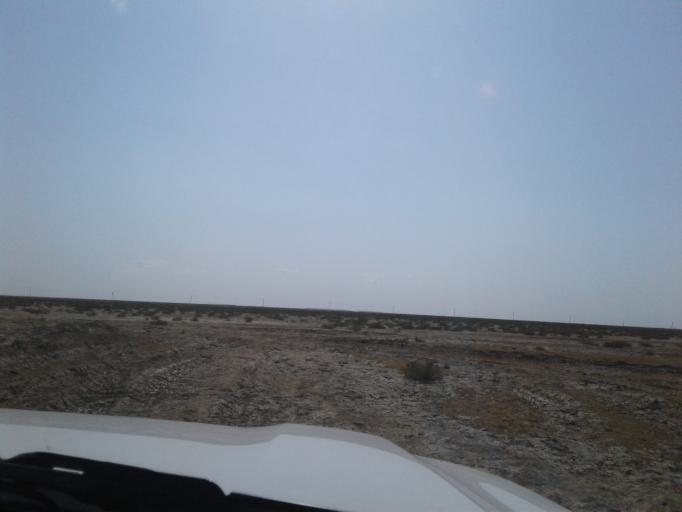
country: TM
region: Balkan
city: Gumdag
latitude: 38.3590
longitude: 54.5237
